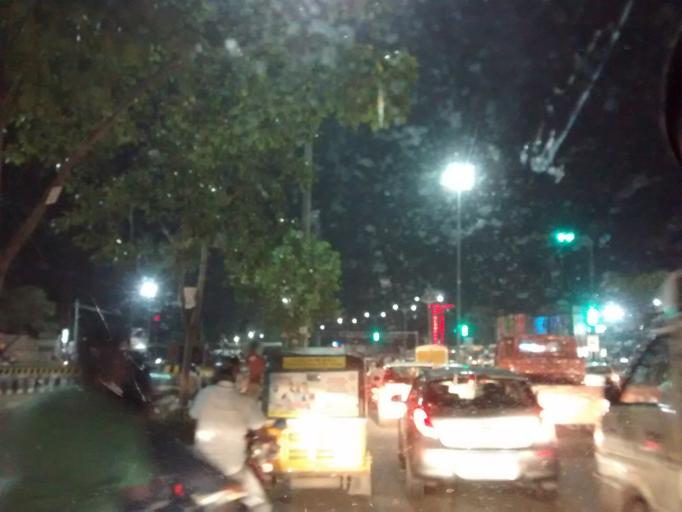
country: IN
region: Telangana
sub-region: Hyderabad
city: Hyderabad
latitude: 17.3215
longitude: 78.4314
